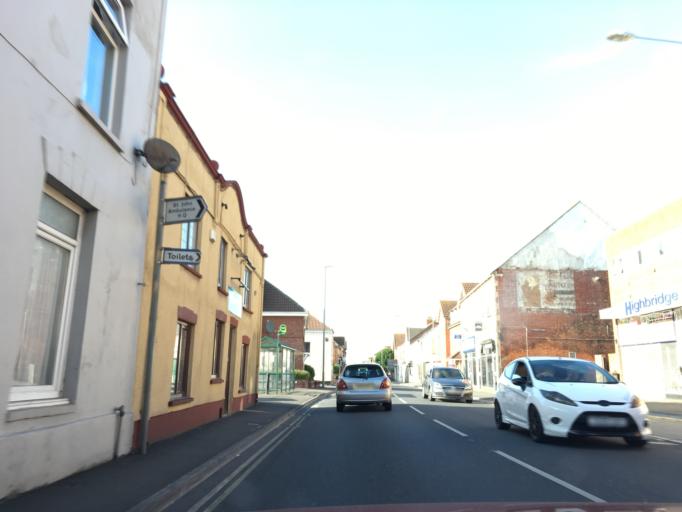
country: GB
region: England
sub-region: Somerset
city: Highbridge
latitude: 51.2200
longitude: -2.9760
